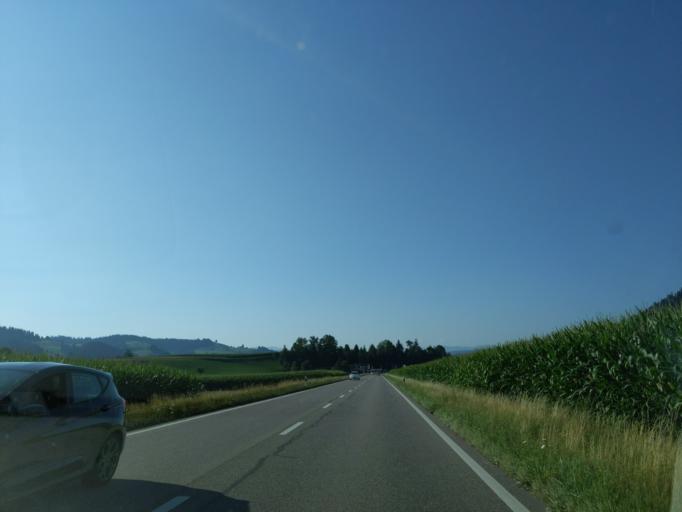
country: CH
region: Bern
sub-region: Emmental District
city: Ruderswil
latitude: 46.9836
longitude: 7.7386
